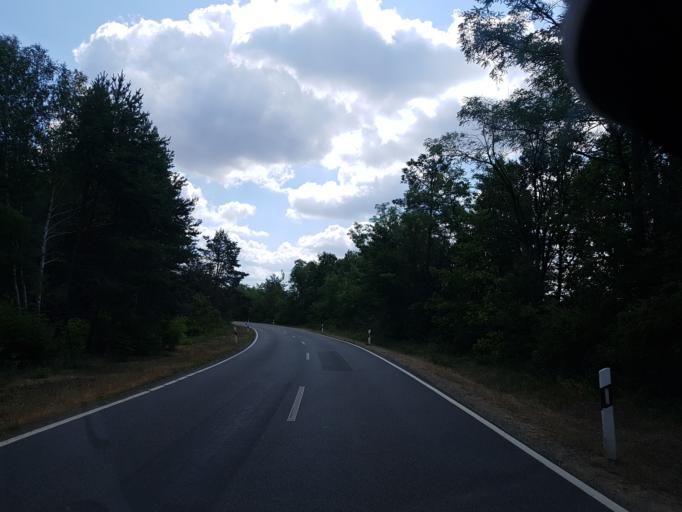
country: DE
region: Brandenburg
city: Neupetershain
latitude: 51.6795
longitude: 14.1553
